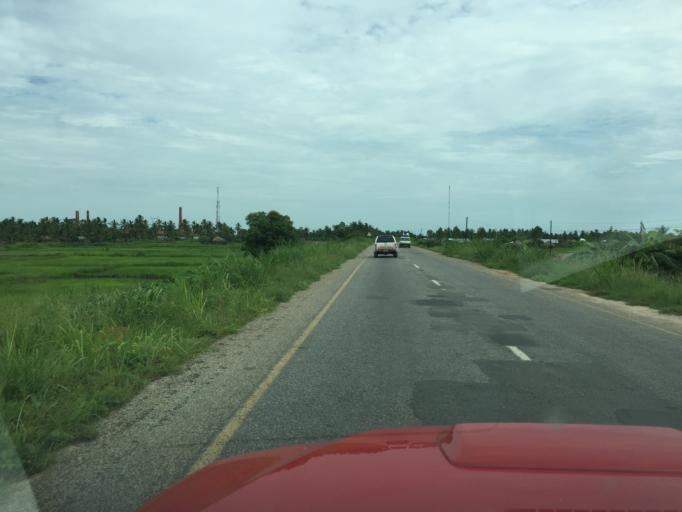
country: MZ
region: Zambezia
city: Quelimane
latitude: -17.7204
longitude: 36.8972
